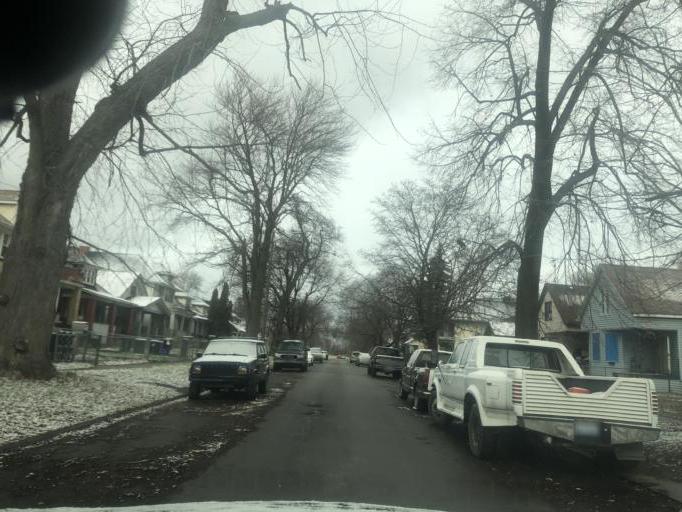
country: US
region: Michigan
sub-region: Wayne County
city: River Rouge
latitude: 42.3110
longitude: -83.1114
